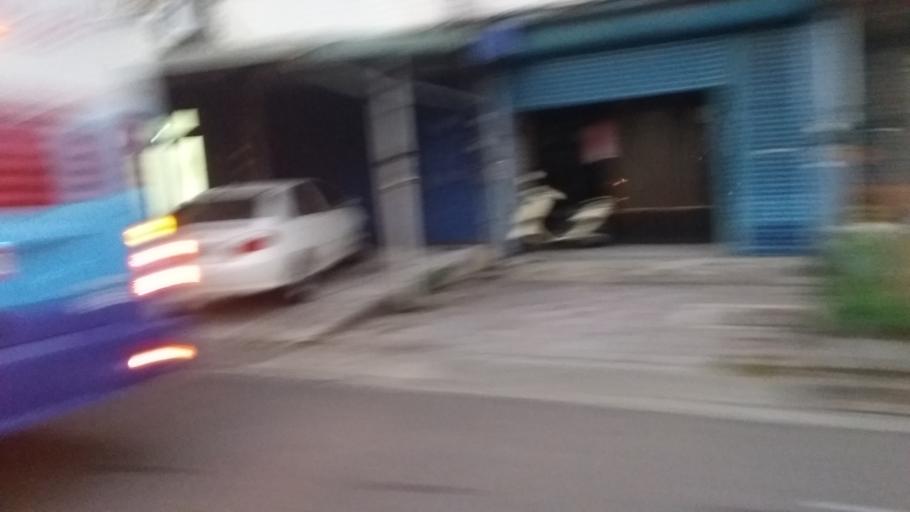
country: TW
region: Taiwan
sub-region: Hsinchu
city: Hsinchu
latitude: 24.7338
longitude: 120.9137
